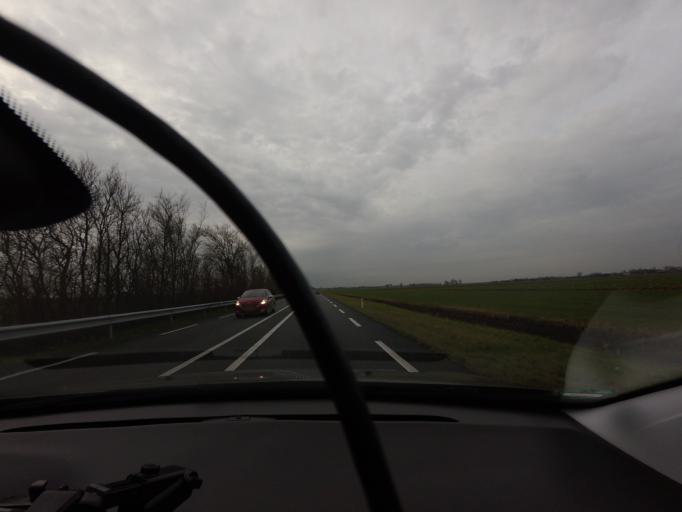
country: NL
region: North Holland
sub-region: Gemeente Hollands Kroon
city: Den Oever
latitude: 52.9215
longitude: 5.0095
